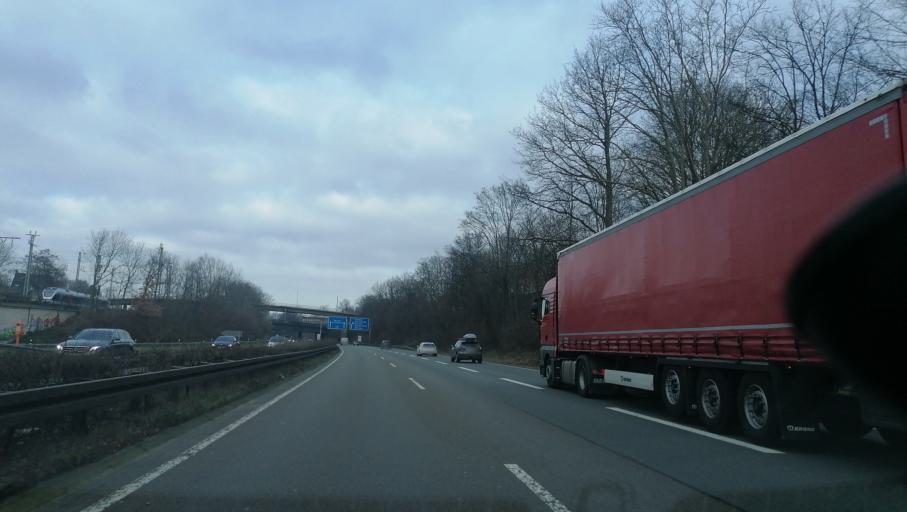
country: DE
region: North Rhine-Westphalia
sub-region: Regierungsbezirk Arnsberg
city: Herne
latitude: 51.5349
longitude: 7.2106
